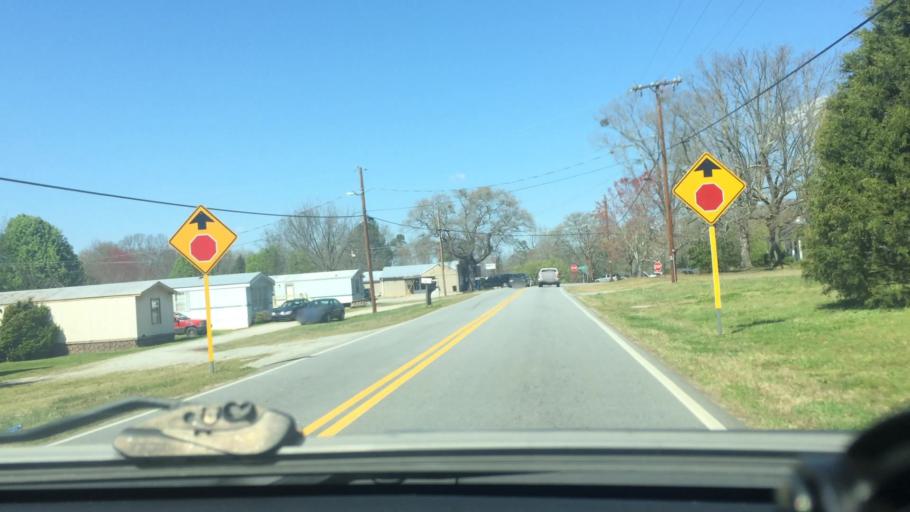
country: US
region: South Carolina
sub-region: Anderson County
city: Powdersville
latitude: 34.7875
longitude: -82.4909
